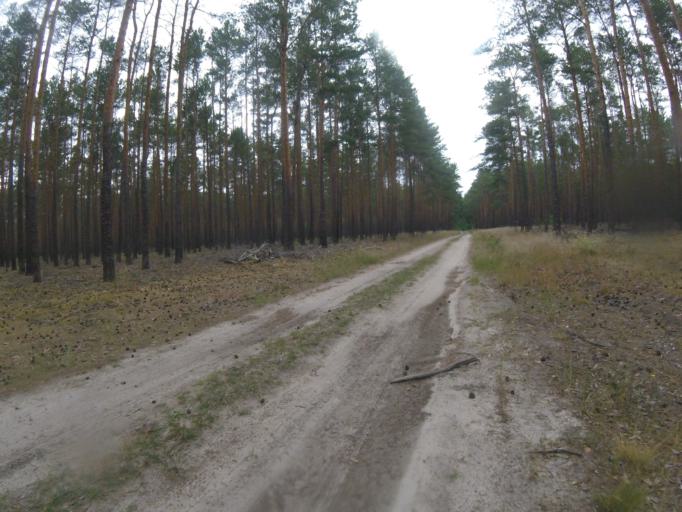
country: DE
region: Brandenburg
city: Gross Koris
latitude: 52.1909
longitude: 13.6604
